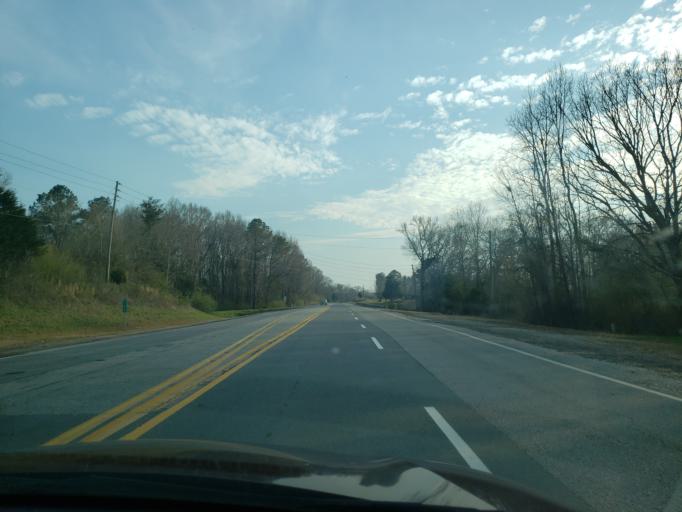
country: US
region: Alabama
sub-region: Hale County
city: Moundville
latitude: 32.9405
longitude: -87.6280
